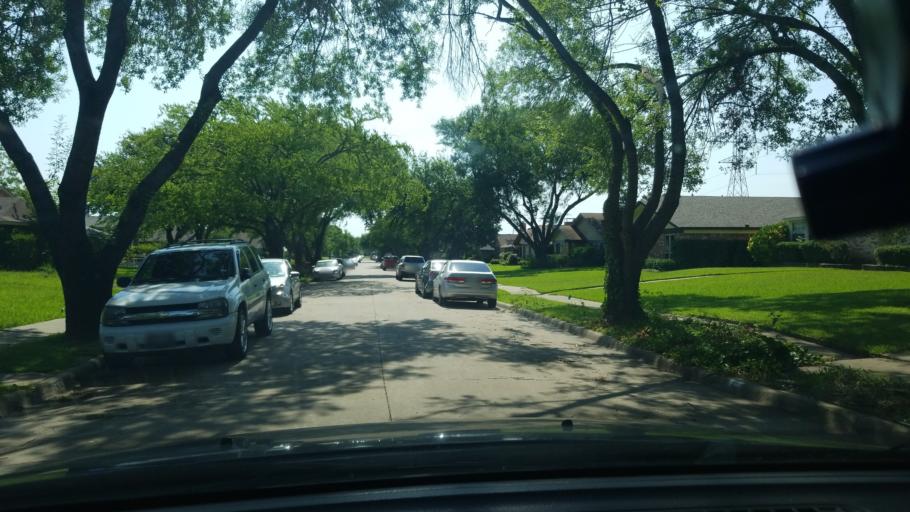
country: US
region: Texas
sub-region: Dallas County
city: Mesquite
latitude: 32.8202
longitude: -96.6232
